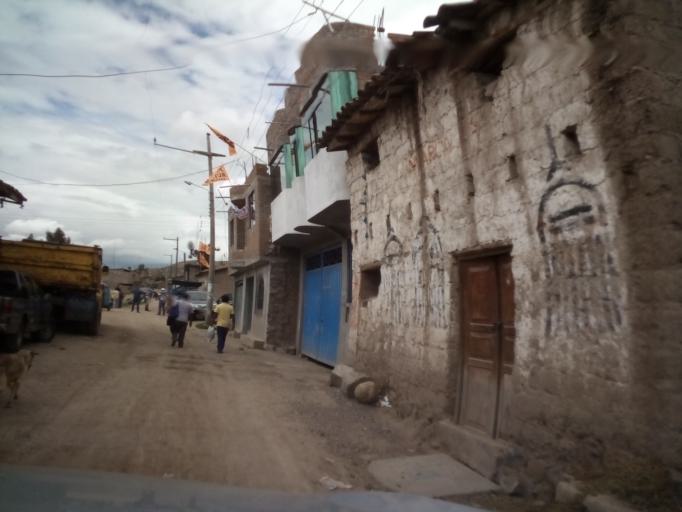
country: PE
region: Ayacucho
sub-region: Provincia de Huamanga
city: Ayacucho
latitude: -13.1663
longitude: -74.2489
